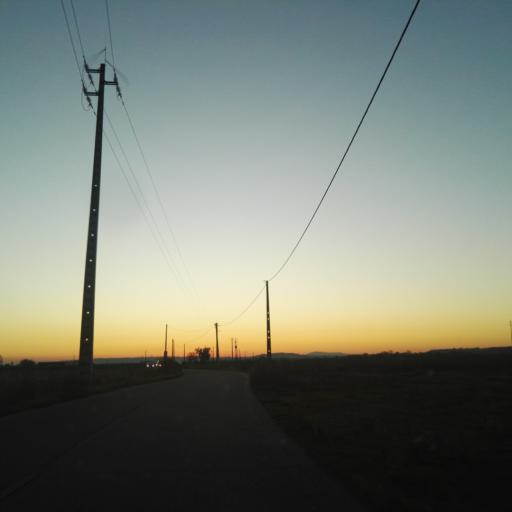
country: PT
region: Santarem
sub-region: Alpiarca
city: Alpiarca
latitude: 39.2907
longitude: -8.5856
